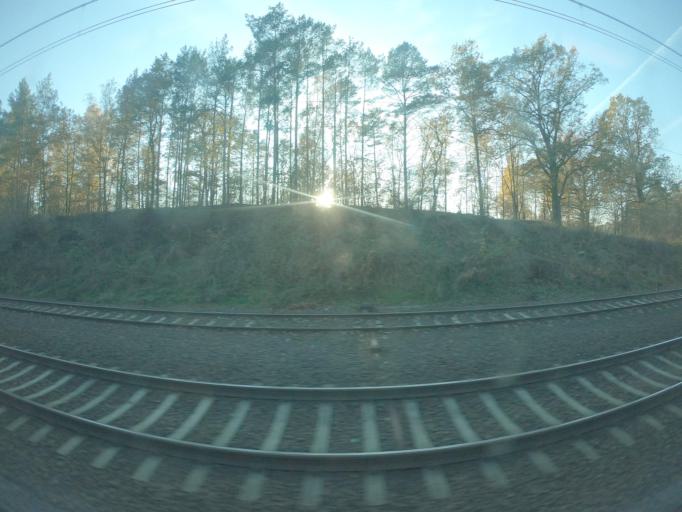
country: PL
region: Lubusz
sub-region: Powiat sulecinski
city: Torzym
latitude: 52.2485
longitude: 14.9603
